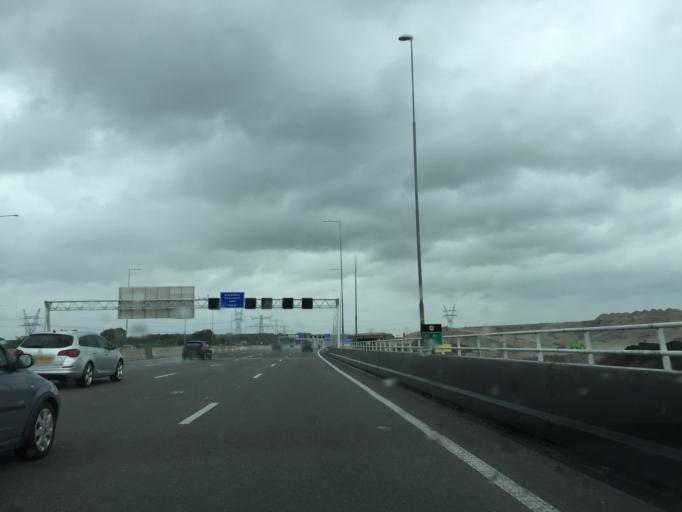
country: NL
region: North Holland
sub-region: Gemeente Amsterdam
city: Driemond
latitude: 52.3323
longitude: 5.0161
